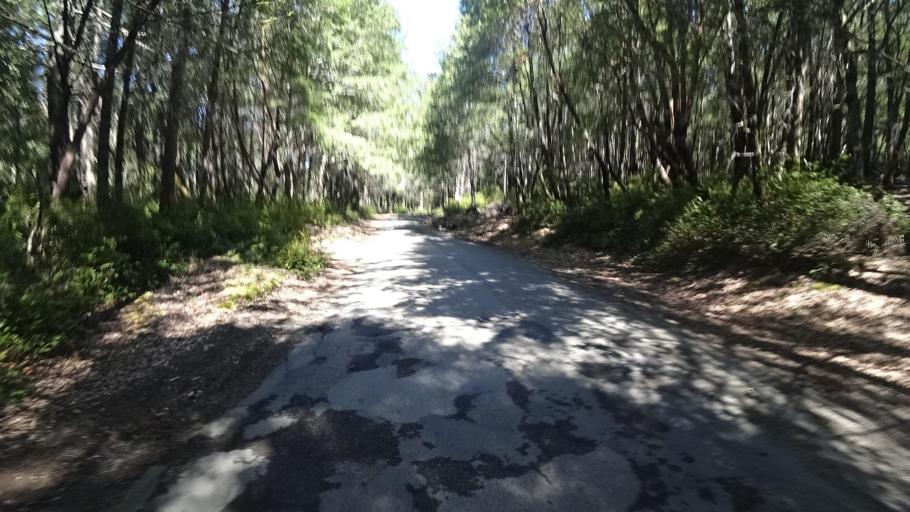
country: US
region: California
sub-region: Humboldt County
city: Redway
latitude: 40.2030
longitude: -124.1024
